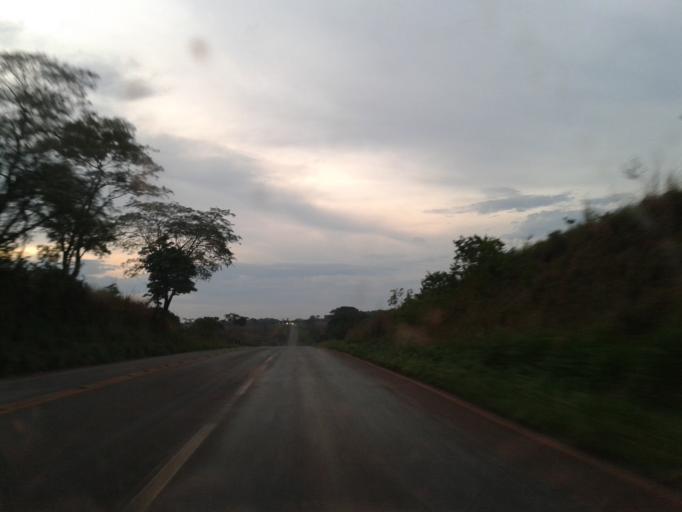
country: BR
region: Goias
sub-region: Santa Helena De Goias
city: Santa Helena de Goias
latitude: -17.8735
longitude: -50.7263
